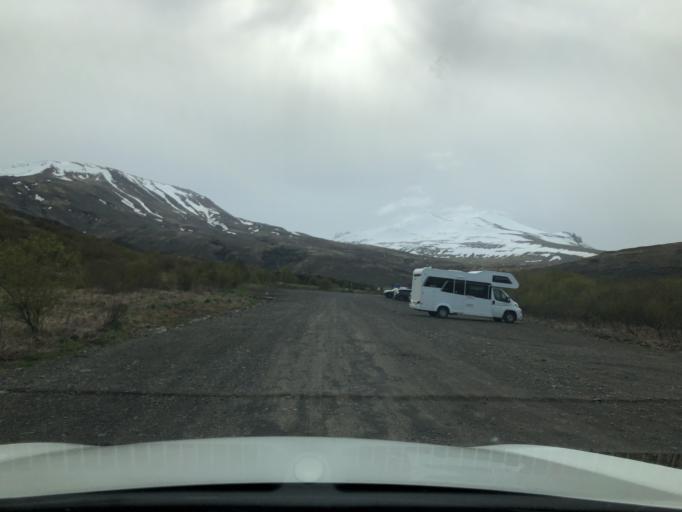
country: IS
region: South
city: Hveragerdi
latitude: 64.3855
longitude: -21.2953
